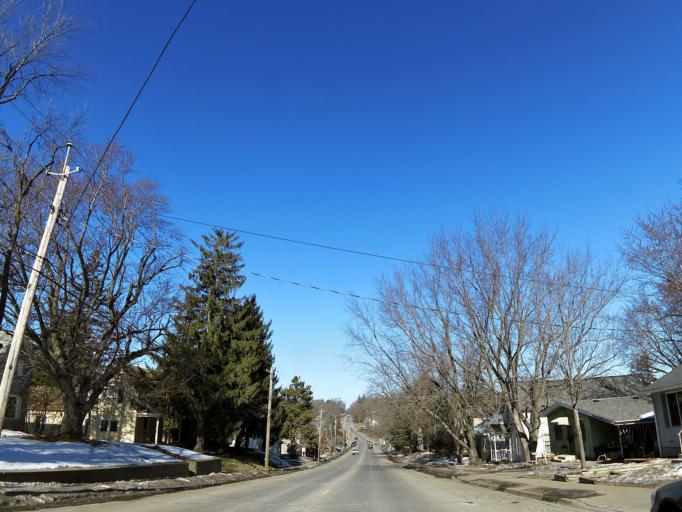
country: US
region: Minnesota
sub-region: Washington County
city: Stillwater
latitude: 45.0575
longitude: -92.8204
